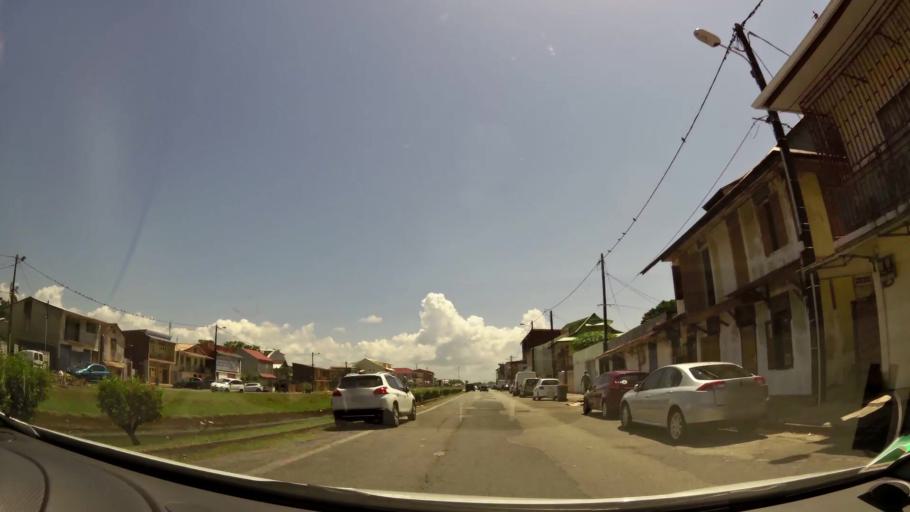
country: GF
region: Guyane
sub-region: Guyane
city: Cayenne
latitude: 4.9365
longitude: -52.3287
